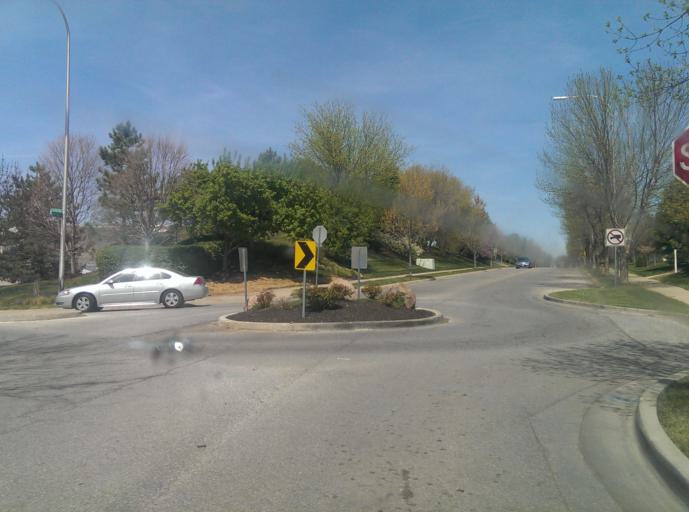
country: US
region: Missouri
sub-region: Jackson County
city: Grandview
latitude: 38.8865
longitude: -94.6038
